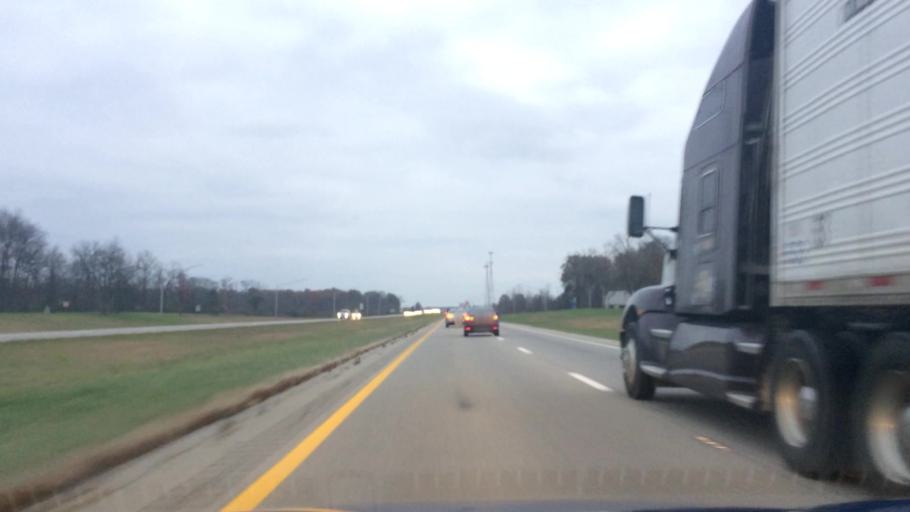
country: US
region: Ohio
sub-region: Union County
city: New California
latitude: 40.2024
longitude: -83.2865
